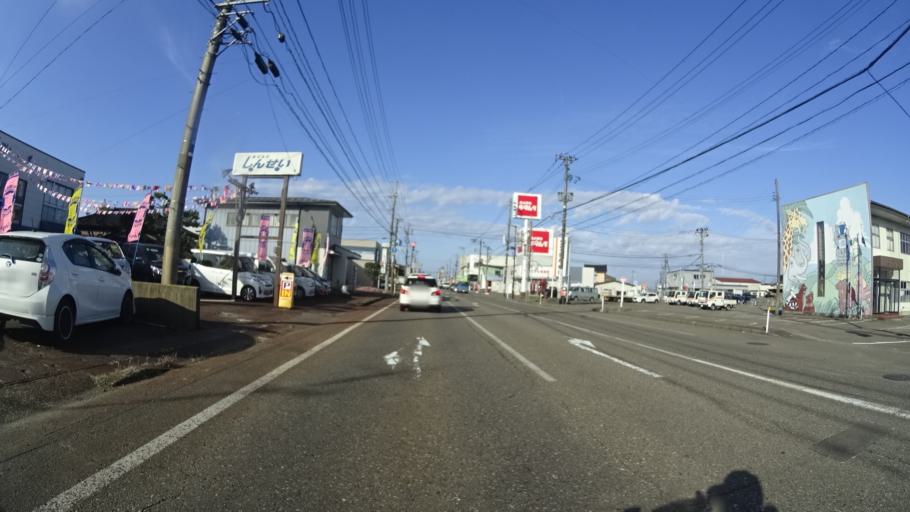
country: JP
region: Niigata
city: Joetsu
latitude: 37.1568
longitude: 138.2380
